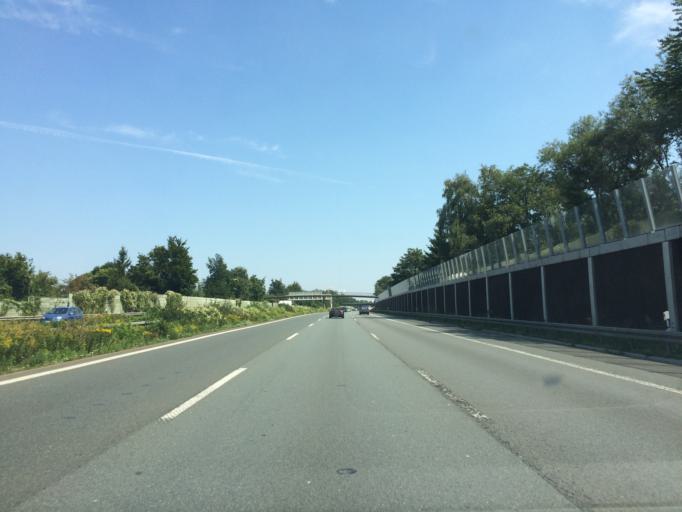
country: DE
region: North Rhine-Westphalia
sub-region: Regierungsbezirk Munster
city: Recklinghausen
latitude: 51.5894
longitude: 7.2269
